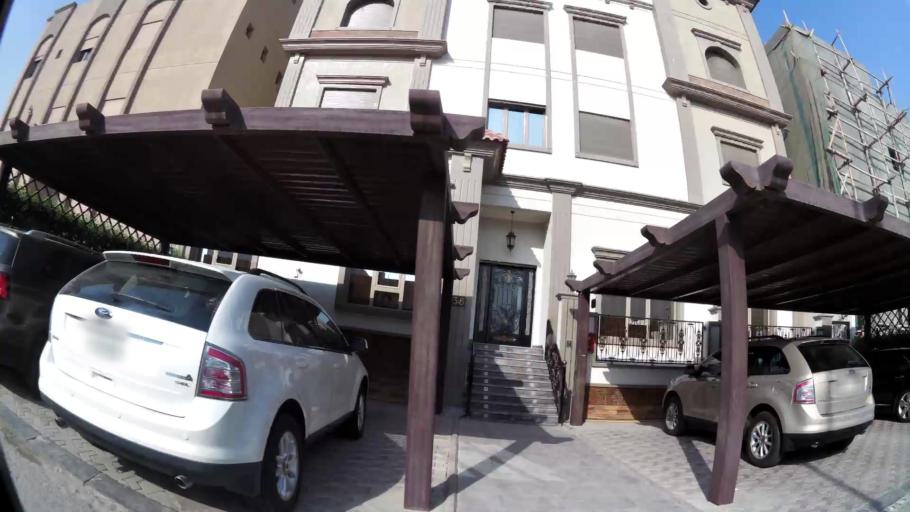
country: KW
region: Al Asimah
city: Ar Rabiyah
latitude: 29.3059
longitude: 47.7986
